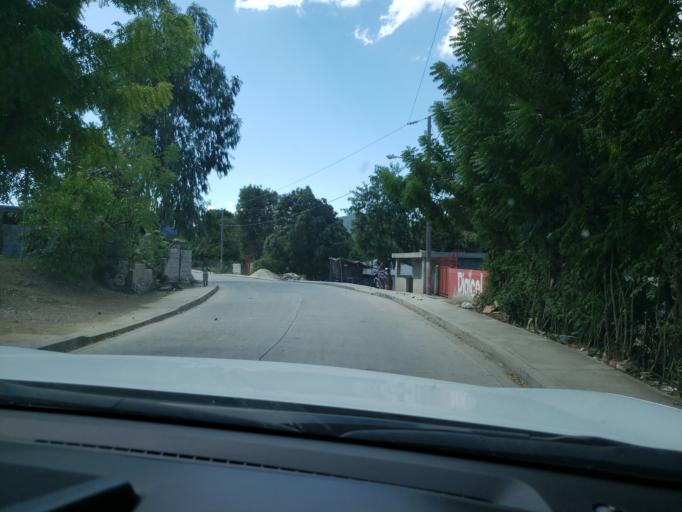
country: HT
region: Grandans
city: Anse-a-Veau
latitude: 18.4504
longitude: -73.3831
